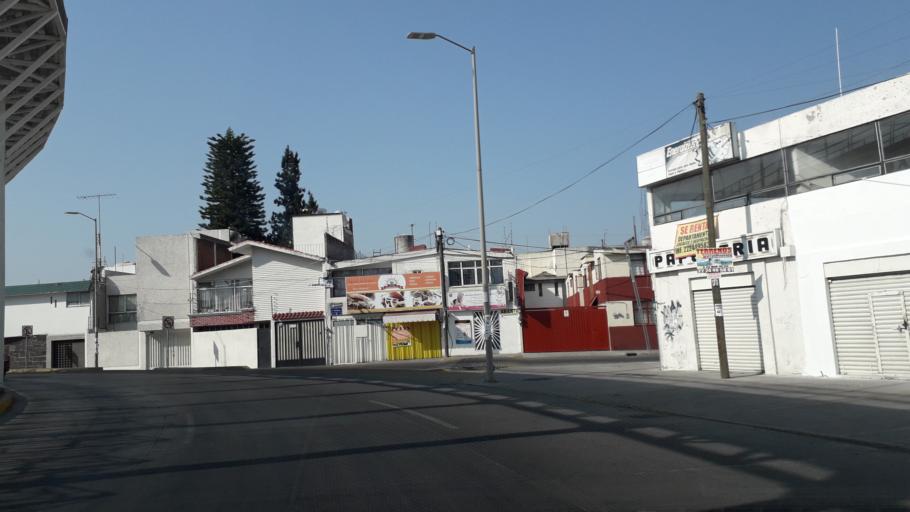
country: MX
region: Puebla
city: Puebla
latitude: 19.0583
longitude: -98.2200
